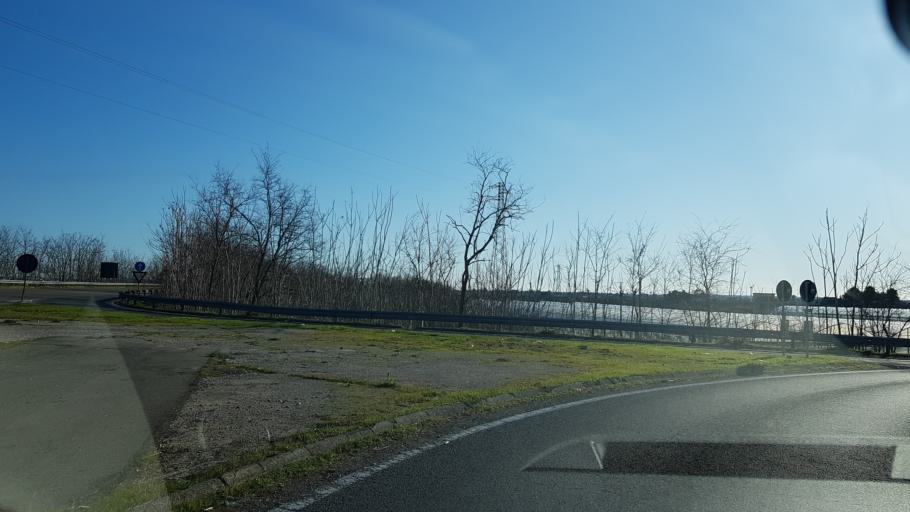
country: IT
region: Apulia
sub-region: Provincia di Lecce
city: Taviano
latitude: 39.9926
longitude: 18.1003
